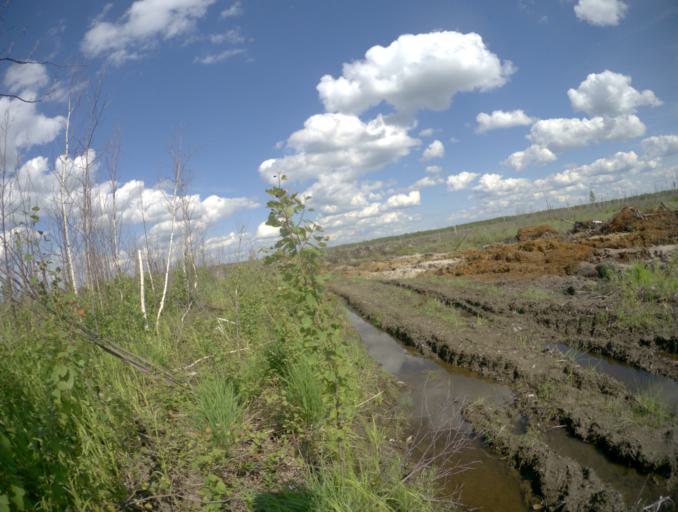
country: RU
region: Vladimir
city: Velikodvorskiy
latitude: 55.3081
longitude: 40.9075
